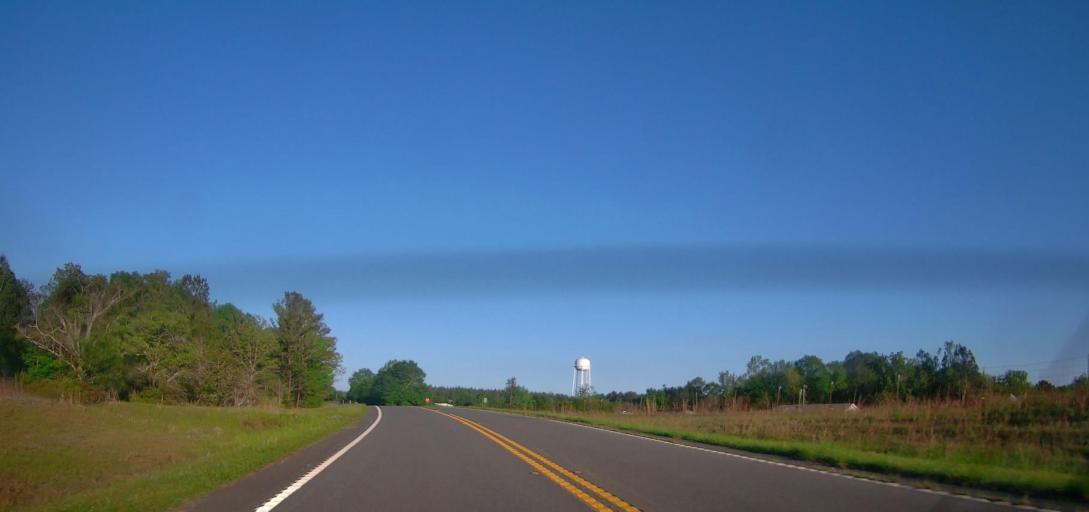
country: US
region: Georgia
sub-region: Schley County
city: Ellaville
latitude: 32.3459
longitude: -84.3714
